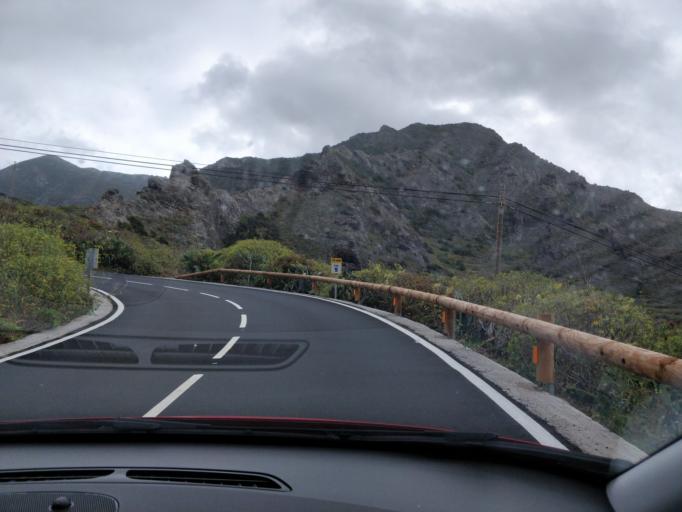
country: ES
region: Canary Islands
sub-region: Provincia de Santa Cruz de Tenerife
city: Tanque
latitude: 28.3491
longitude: -16.8446
